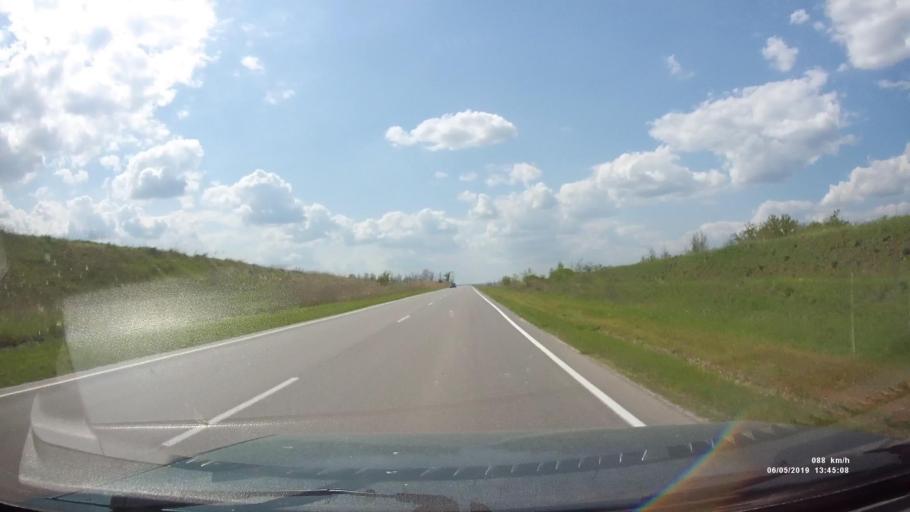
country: RU
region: Rostov
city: Melikhovskaya
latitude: 47.6569
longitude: 40.6062
